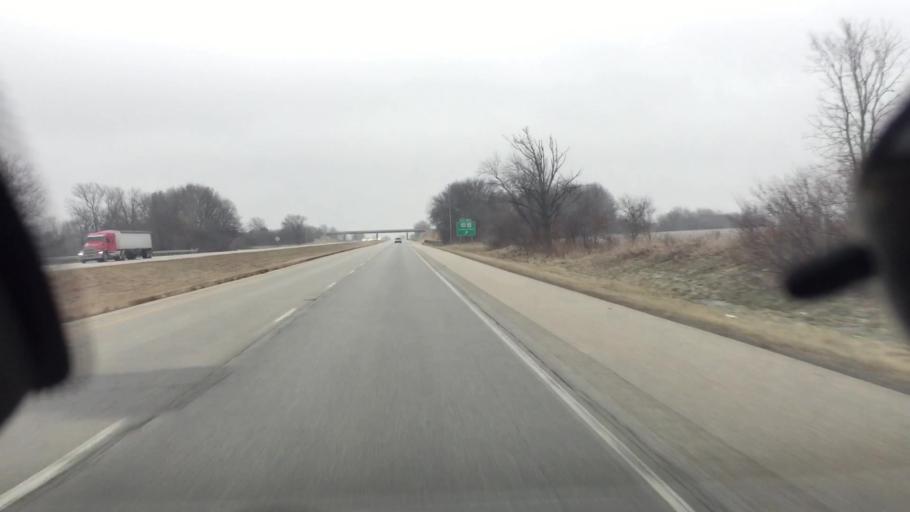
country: US
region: Illinois
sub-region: Knox County
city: Knoxville
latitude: 40.9160
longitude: -90.2519
